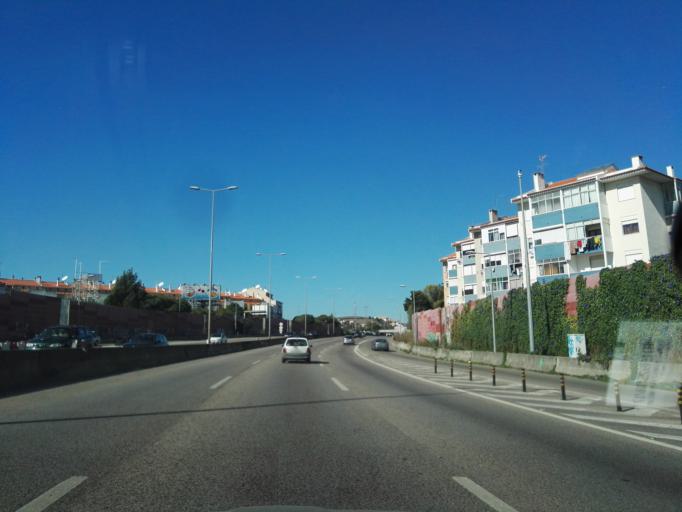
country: PT
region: Lisbon
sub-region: Oeiras
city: Barcarena
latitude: 38.7496
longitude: -9.2843
